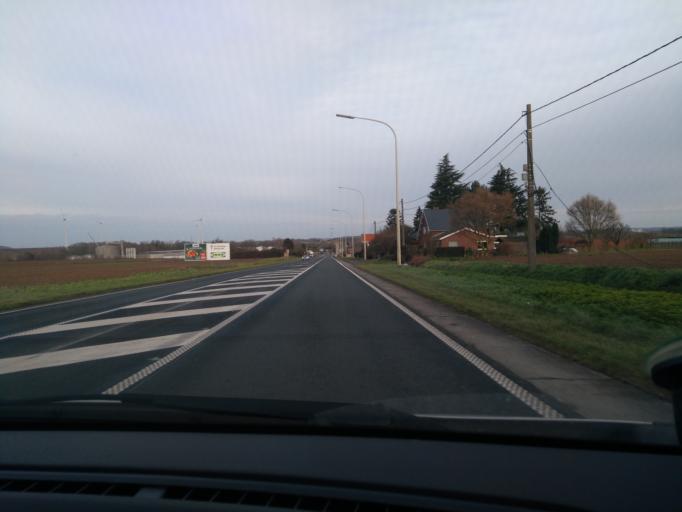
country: BE
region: Wallonia
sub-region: Province du Hainaut
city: Quevy-le-Petit
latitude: 50.3611
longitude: 3.9672
